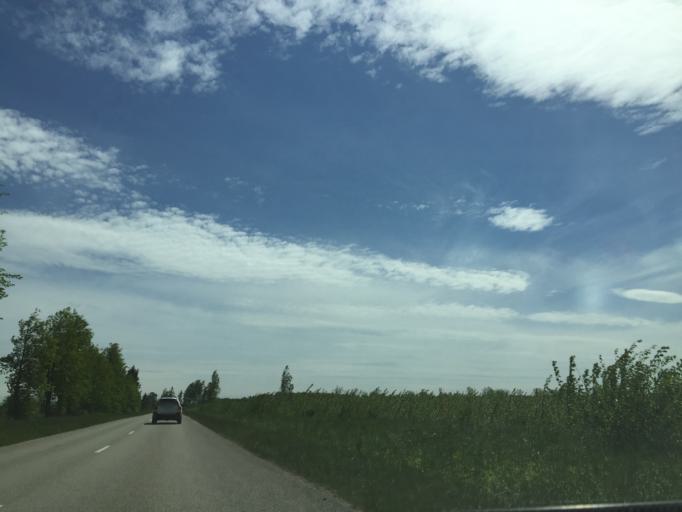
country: LT
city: Linkuva
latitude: 56.0437
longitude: 24.1241
